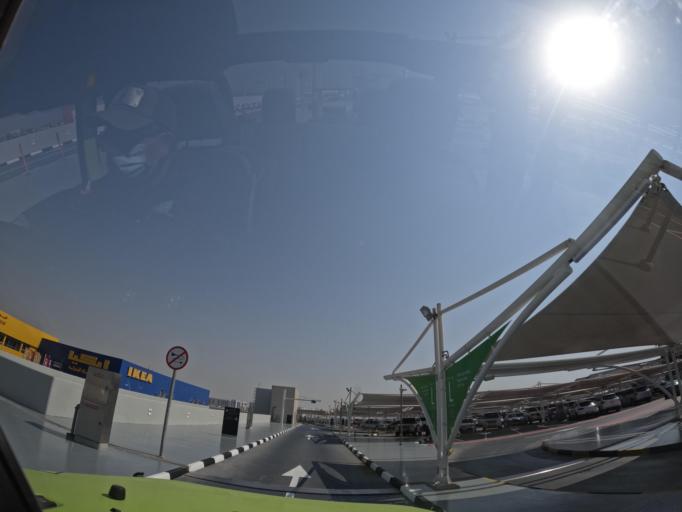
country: AE
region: Abu Dhabi
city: Abu Dhabi
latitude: 24.4902
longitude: 54.6118
